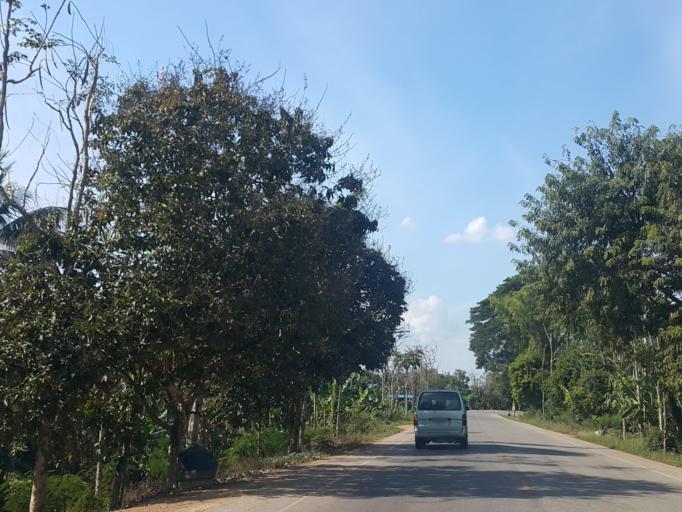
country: TH
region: Sukhothai
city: Sawankhalok
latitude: 17.2569
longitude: 99.8388
